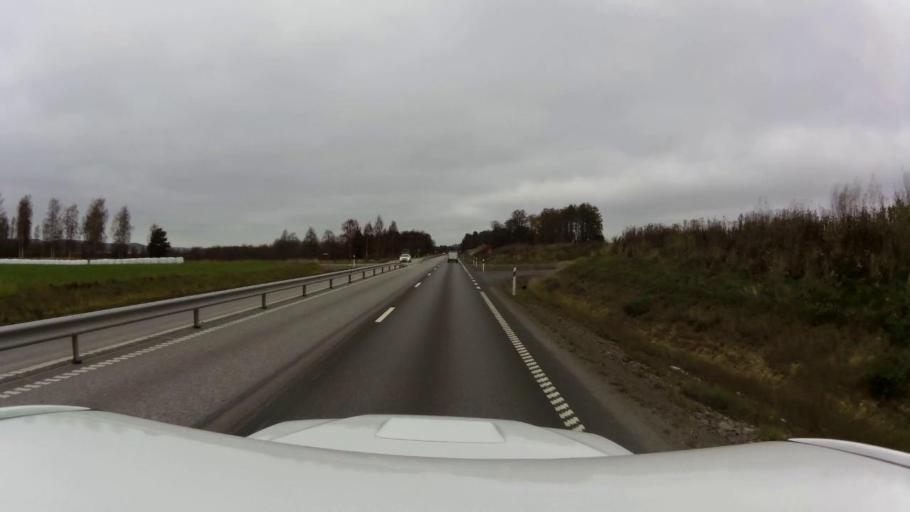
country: SE
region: OEstergoetland
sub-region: Kinda Kommun
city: Rimforsa
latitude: 58.1469
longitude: 15.6807
